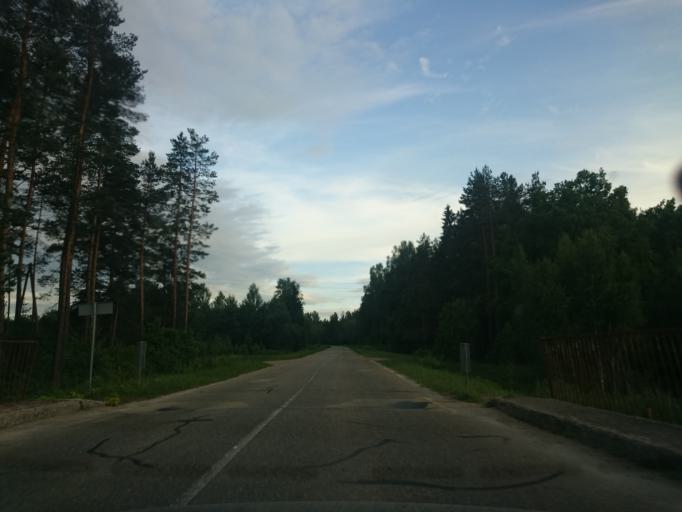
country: LV
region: Incukalns
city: Incukalns
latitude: 57.0290
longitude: 24.6826
